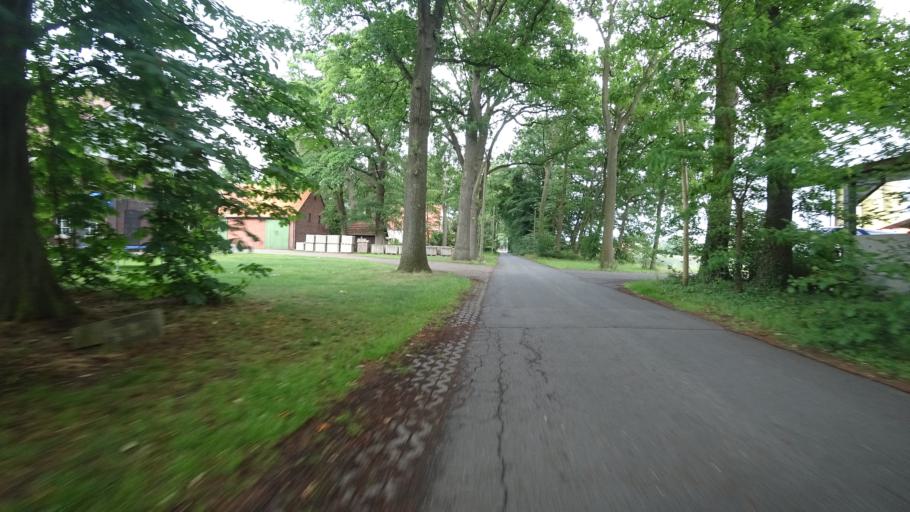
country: DE
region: North Rhine-Westphalia
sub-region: Regierungsbezirk Detmold
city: Guetersloh
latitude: 51.9494
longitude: 8.3619
